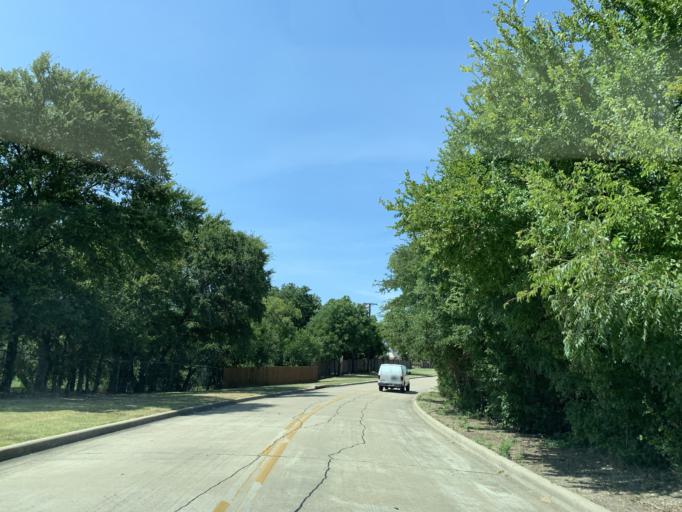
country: US
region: Texas
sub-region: Dallas County
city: Cedar Hill
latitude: 32.6421
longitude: -97.0138
